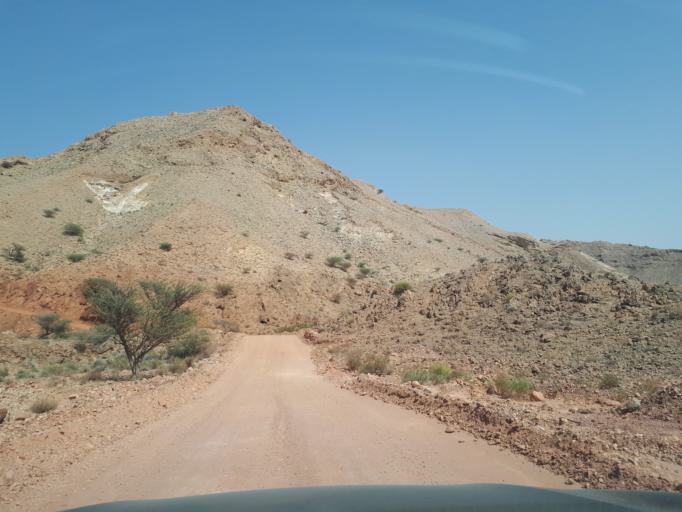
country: OM
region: Ash Sharqiyah
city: Ibra'
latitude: 23.0806
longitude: 58.9287
